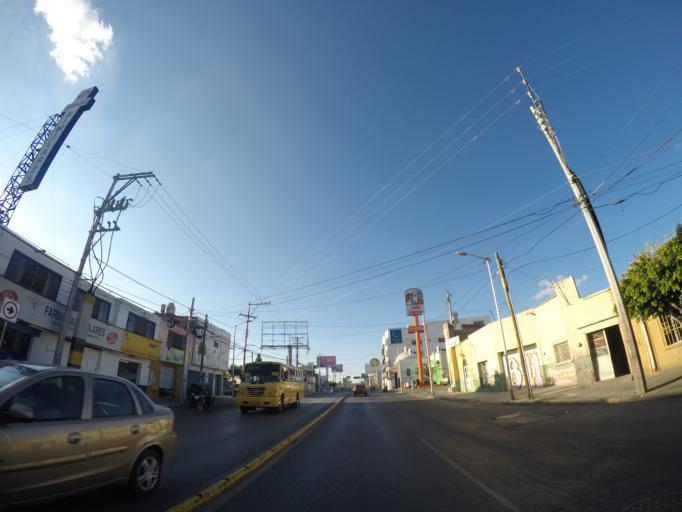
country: MX
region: San Luis Potosi
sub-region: San Luis Potosi
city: San Luis Potosi
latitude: 22.1623
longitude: -101.0006
